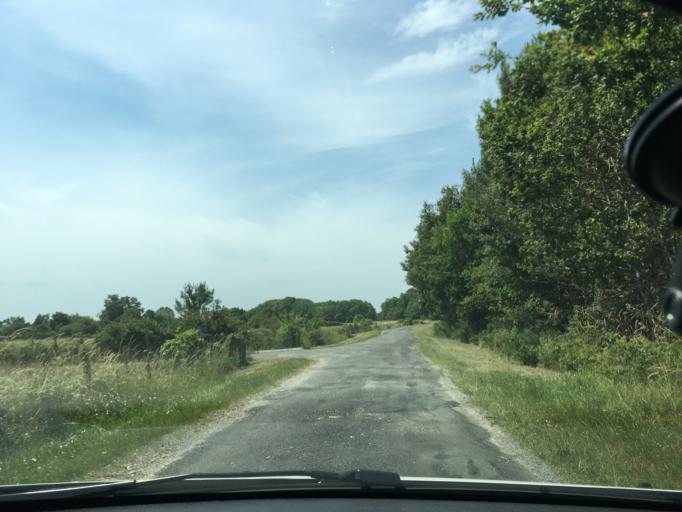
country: FR
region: Aquitaine
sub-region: Departement de la Gironde
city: Lesparre-Medoc
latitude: 45.2777
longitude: -0.9119
